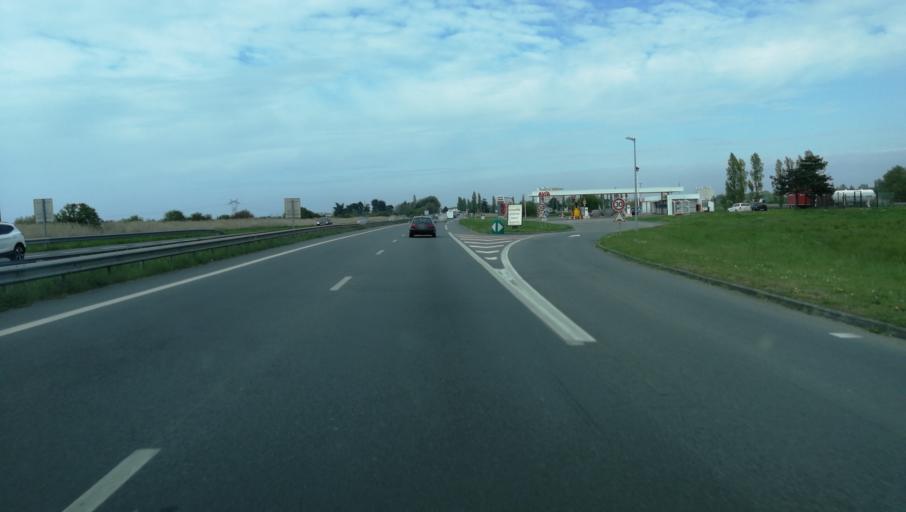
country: FR
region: Pays de la Loire
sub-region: Departement de la Loire-Atlantique
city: Trignac
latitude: 47.3105
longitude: -2.2019
